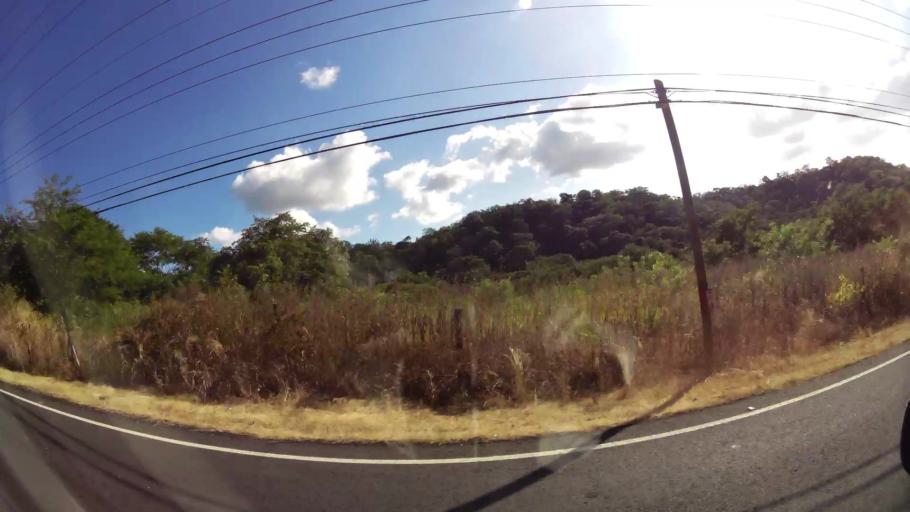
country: CR
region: Guanacaste
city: Sardinal
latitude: 10.5873
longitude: -85.6462
